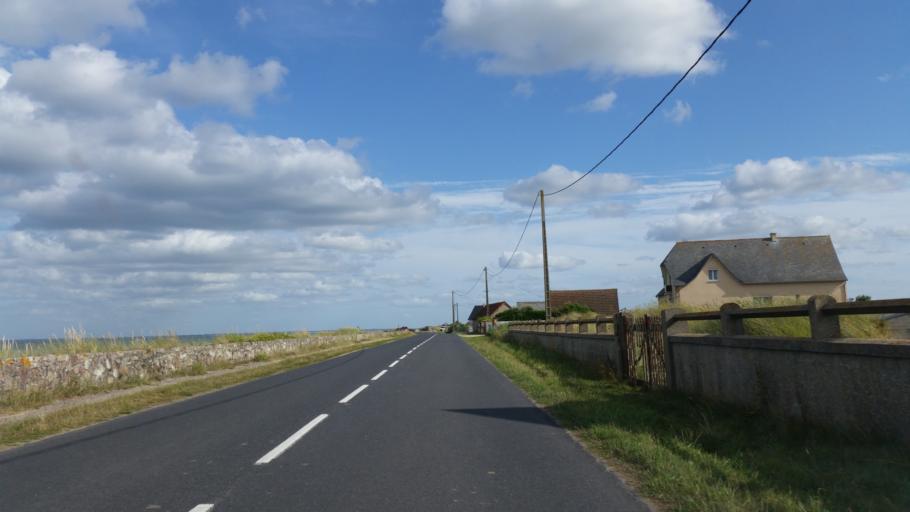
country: FR
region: Lower Normandy
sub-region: Departement de la Manche
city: Sainte-Mere-Eglise
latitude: 49.4556
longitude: -1.2230
